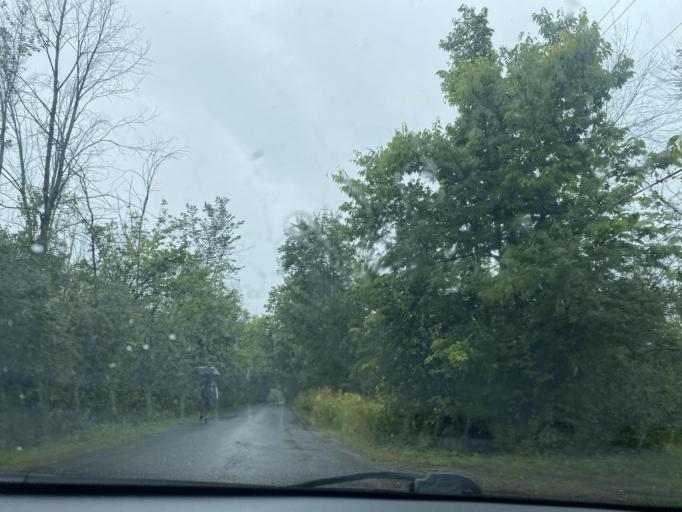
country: CA
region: Quebec
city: Baie-D'Urfe
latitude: 45.4670
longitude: -73.9254
